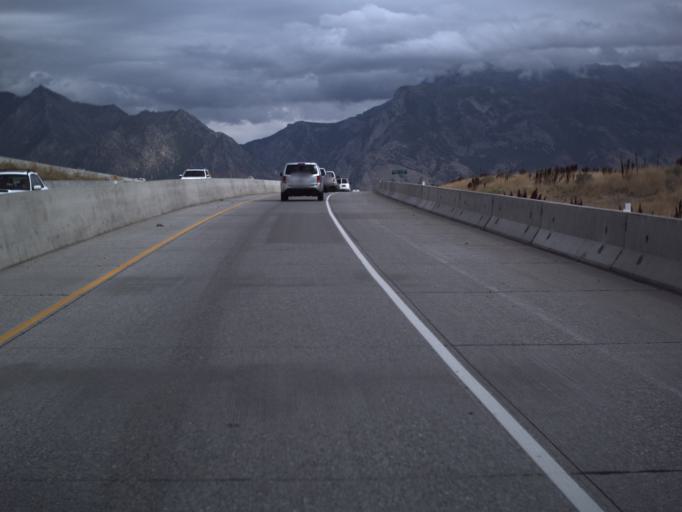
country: US
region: Utah
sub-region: Utah County
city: Lehi
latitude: 40.4324
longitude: -111.8668
